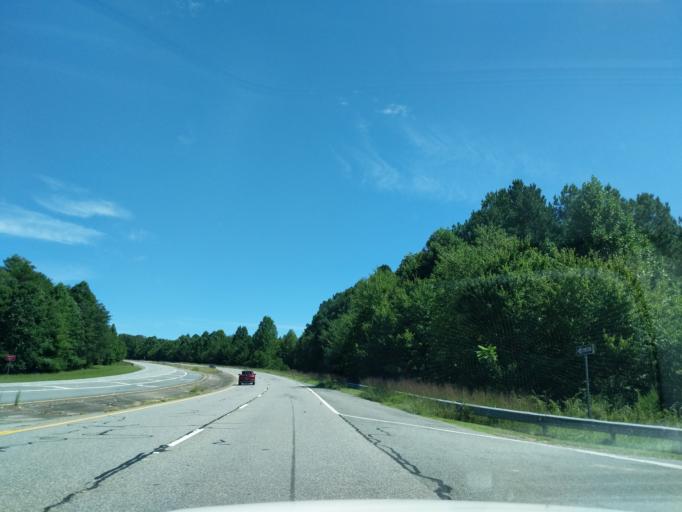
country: US
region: Georgia
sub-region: Fannin County
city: Blue Ridge
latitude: 34.8887
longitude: -84.2092
